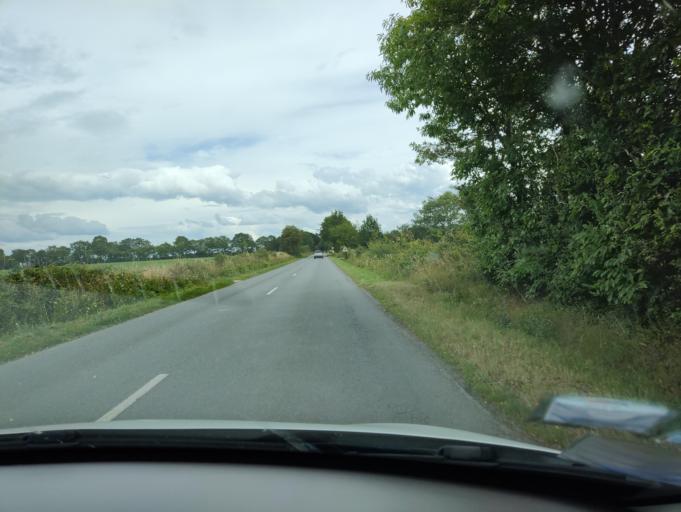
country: FR
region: Pays de la Loire
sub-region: Departement de la Loire-Atlantique
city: Chateaubriant
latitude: 47.7088
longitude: -1.4198
